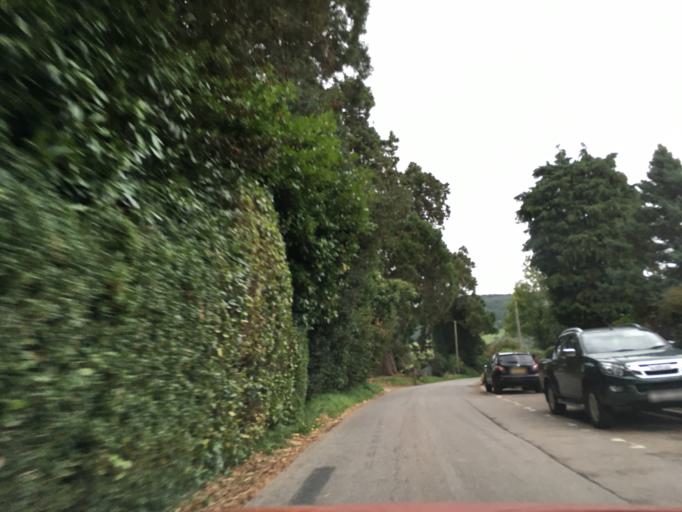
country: GB
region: Wales
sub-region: Monmouthshire
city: Llangybi
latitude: 51.6485
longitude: -2.8975
